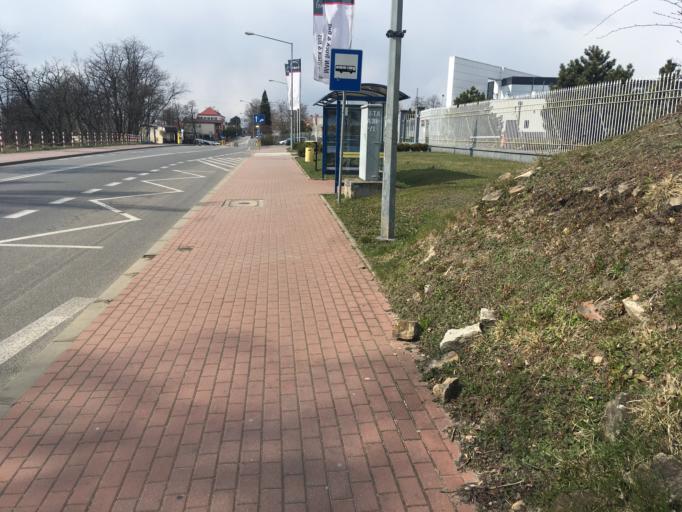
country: PL
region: Swietokrzyskie
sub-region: Powiat starachowicki
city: Starachowice
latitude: 51.0546
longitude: 21.0618
